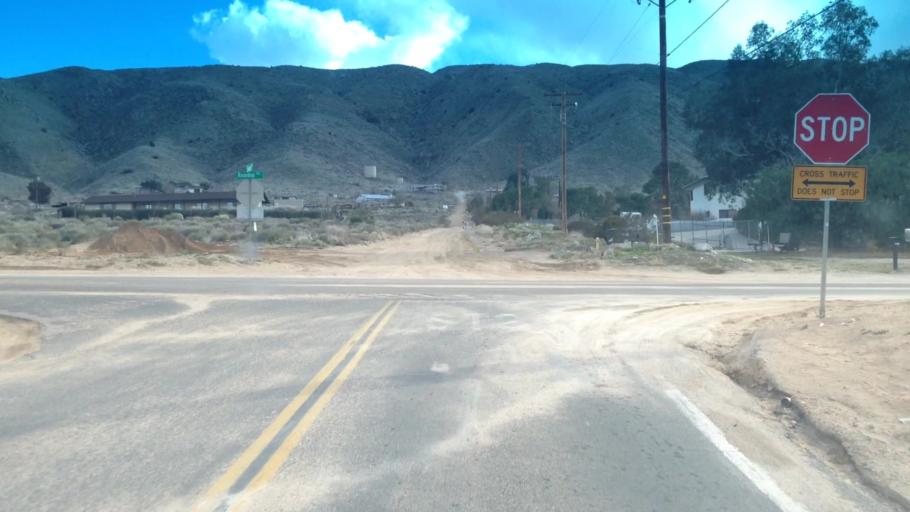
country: US
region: California
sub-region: San Bernardino County
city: Apple Valley
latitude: 34.4212
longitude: -117.1726
